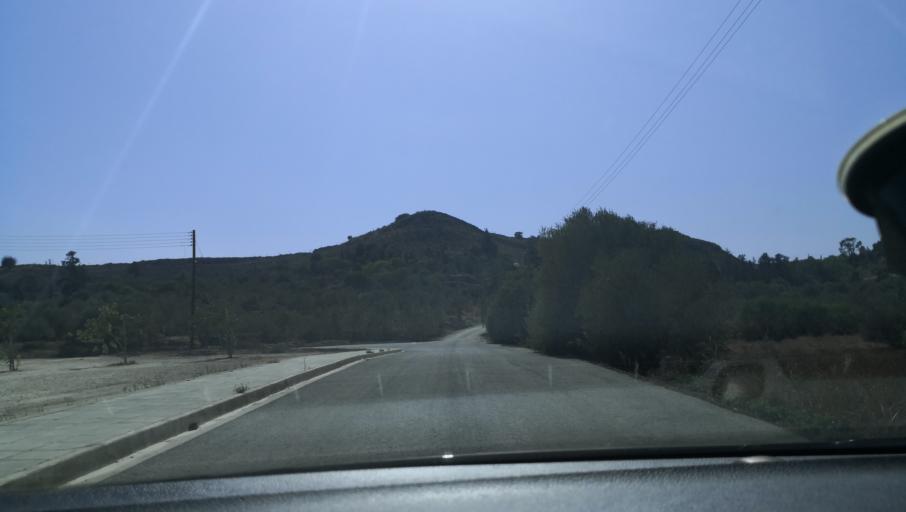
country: CY
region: Lefkosia
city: Mammari
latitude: 35.1728
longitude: 33.2052
